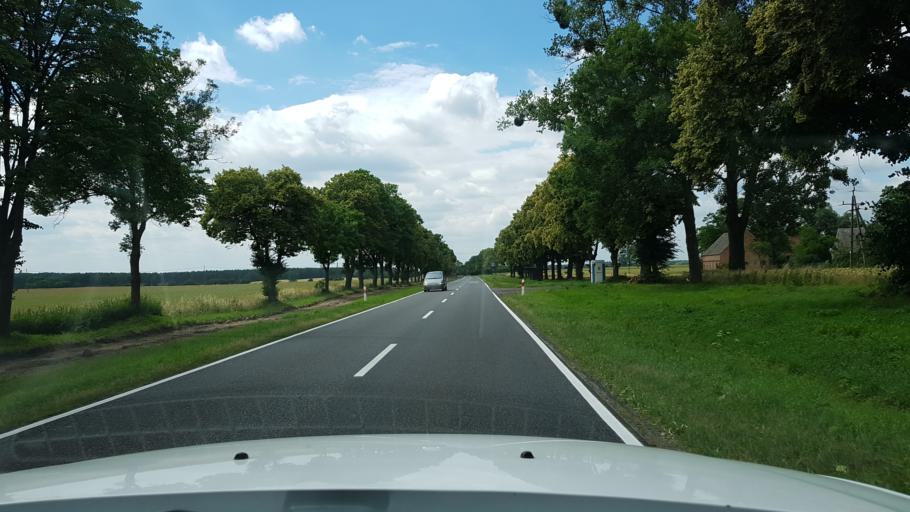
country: PL
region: West Pomeranian Voivodeship
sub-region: Powiat mysliborski
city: Boleszkowice
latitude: 52.7320
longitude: 14.5397
